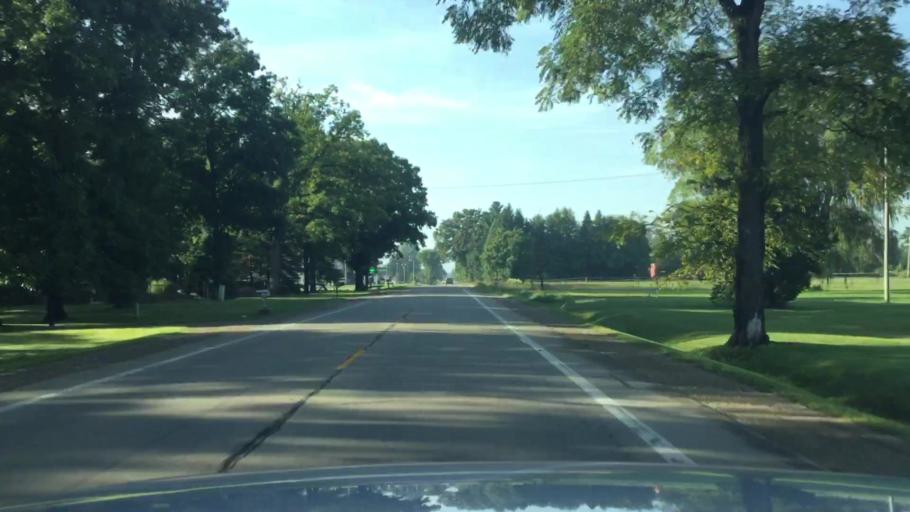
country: US
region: Michigan
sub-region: Lenawee County
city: Manitou Beach-Devils Lake
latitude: 42.0072
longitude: -84.3496
